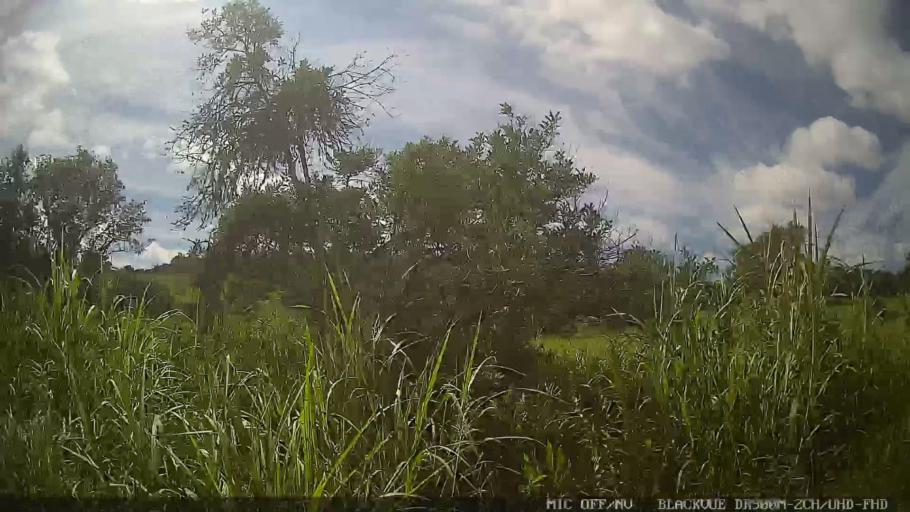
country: BR
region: Sao Paulo
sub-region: Braganca Paulista
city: Braganca Paulista
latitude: -22.9733
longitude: -46.6375
